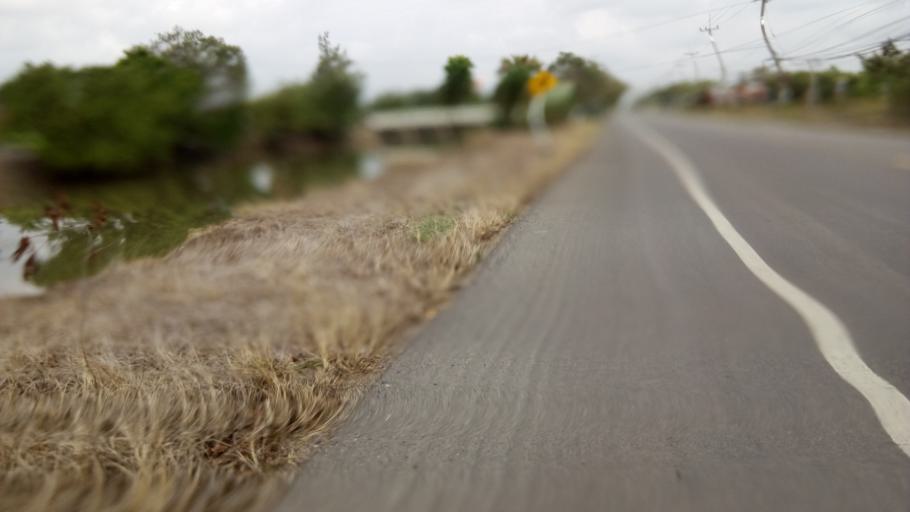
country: TH
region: Pathum Thani
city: Nong Suea
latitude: 14.1676
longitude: 100.8236
